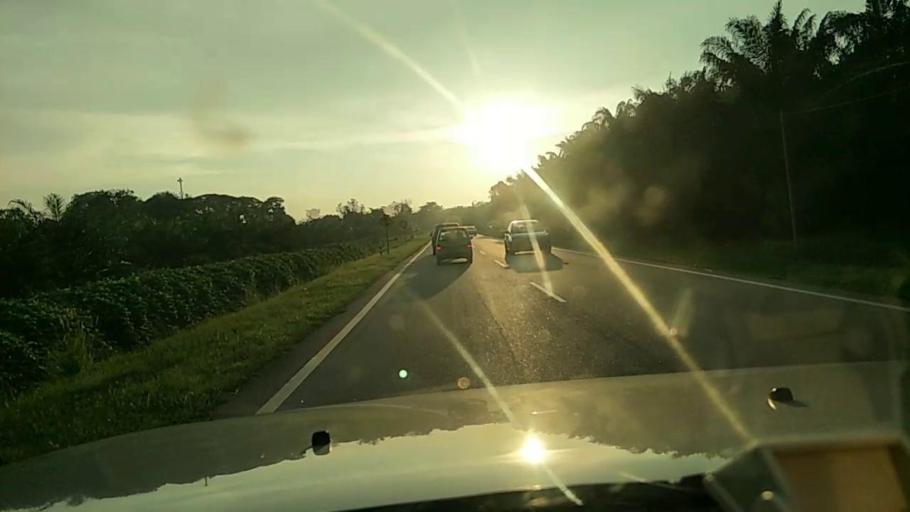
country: MY
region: Selangor
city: Kuala Selangor
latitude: 3.3095
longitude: 101.3216
